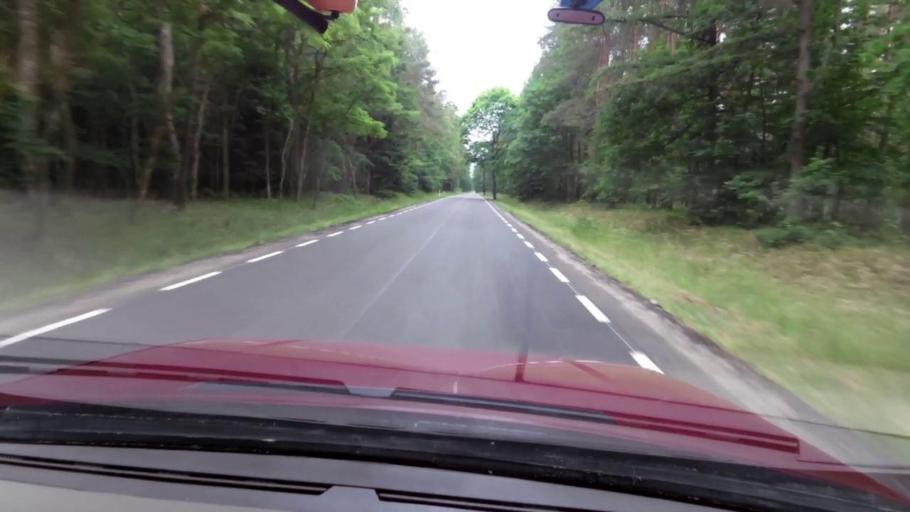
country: PL
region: Pomeranian Voivodeship
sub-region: Powiat slupski
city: Kepice
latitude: 54.2301
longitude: 16.8848
